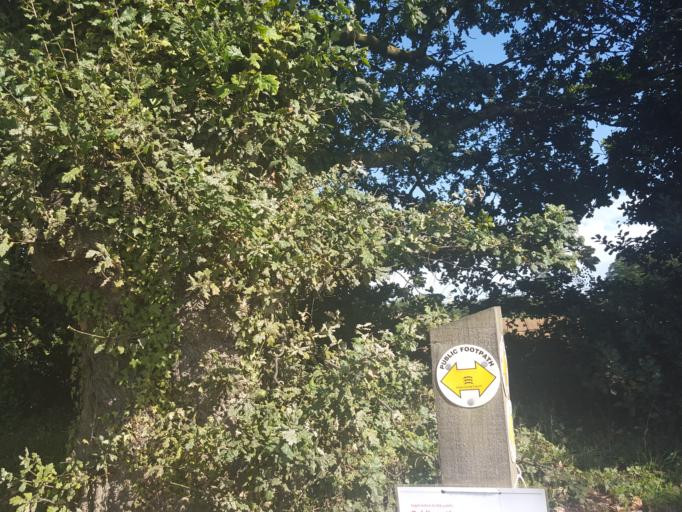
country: GB
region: England
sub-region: Essex
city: Alresford
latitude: 51.8571
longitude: 1.0228
